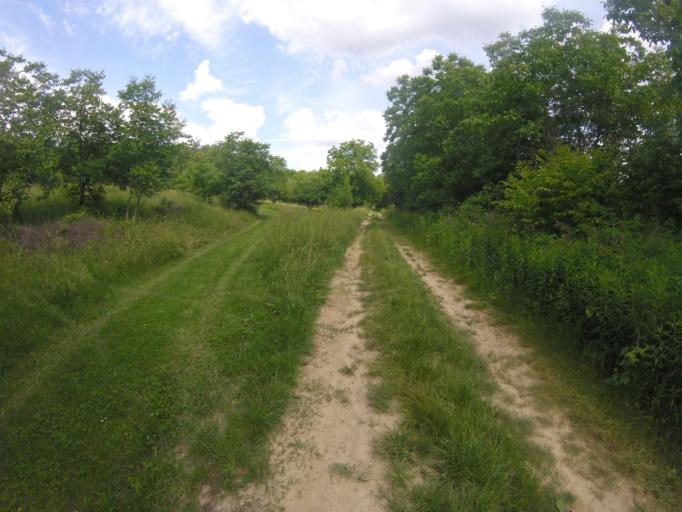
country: HU
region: Zala
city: Zalaszentgrot
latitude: 46.8869
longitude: 17.0392
